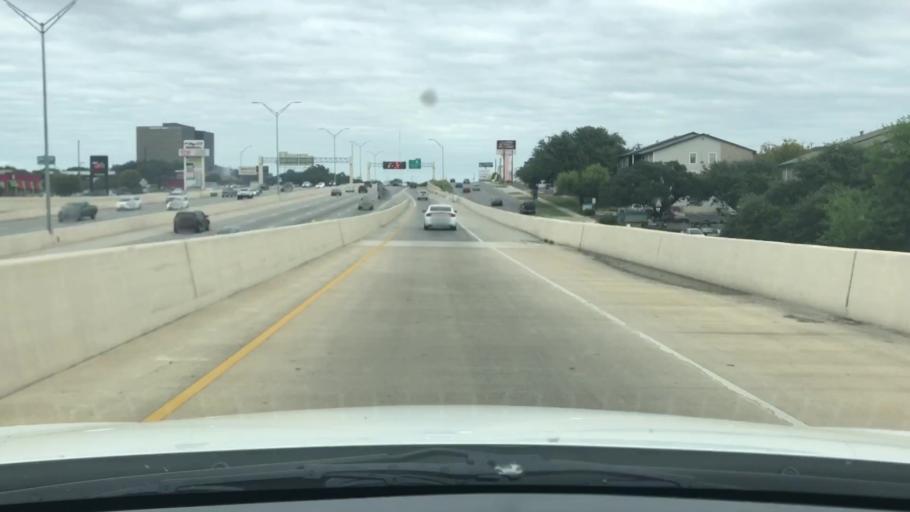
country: US
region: Texas
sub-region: Bexar County
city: Leon Valley
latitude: 29.4871
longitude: -98.5863
